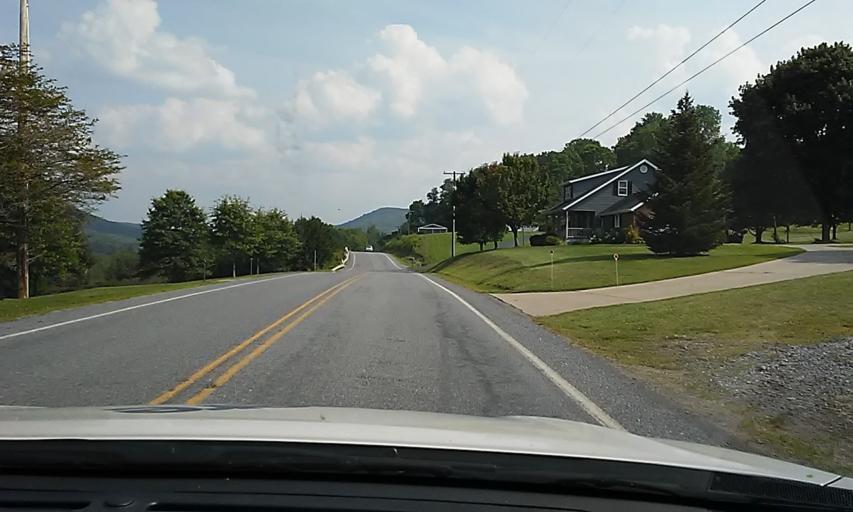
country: US
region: New York
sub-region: Allegany County
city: Wellsville
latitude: 41.9831
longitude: -77.8661
